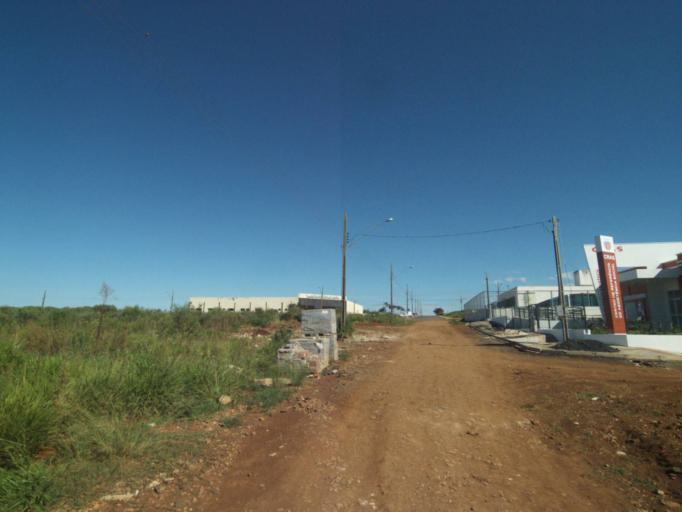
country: BR
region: Parana
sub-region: Pinhao
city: Pinhao
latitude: -25.8366
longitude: -52.0318
